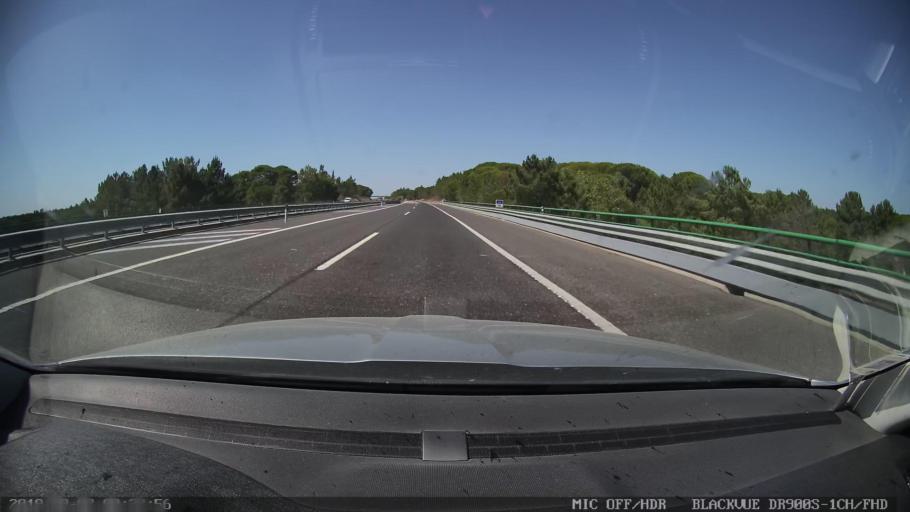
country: PT
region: Evora
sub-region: Vendas Novas
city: Vendas Novas
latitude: 38.6397
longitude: -8.4963
